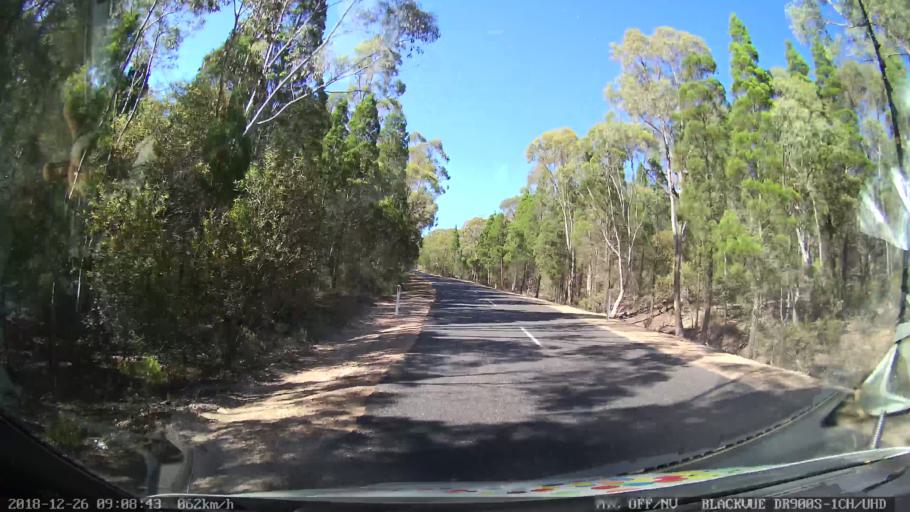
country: AU
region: New South Wales
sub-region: Mid-Western Regional
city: Kandos
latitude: -32.7180
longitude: 150.0001
